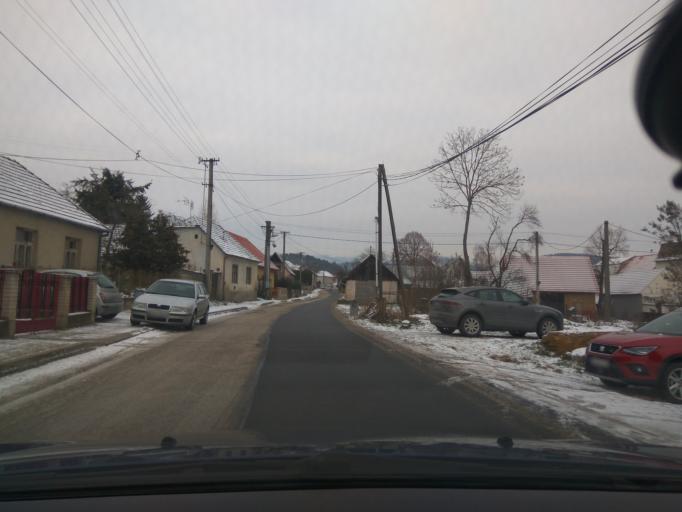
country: SK
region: Nitriansky
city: Stara Tura
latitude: 48.7814
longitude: 17.7370
